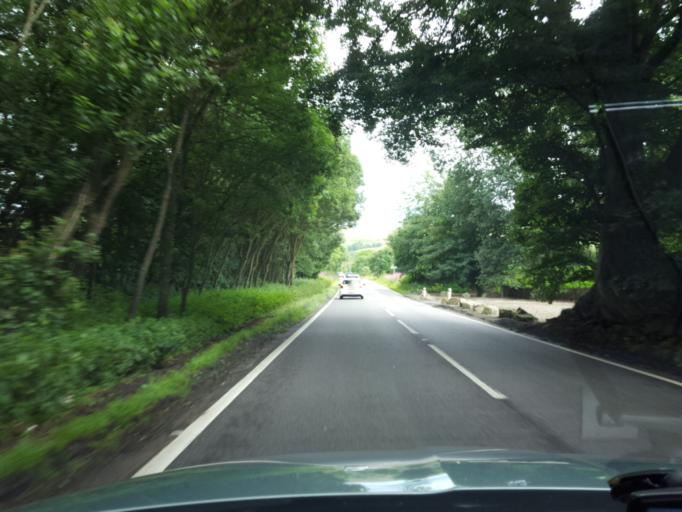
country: GB
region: Scotland
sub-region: Highland
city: Grantown on Spey
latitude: 57.3713
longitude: -3.4803
